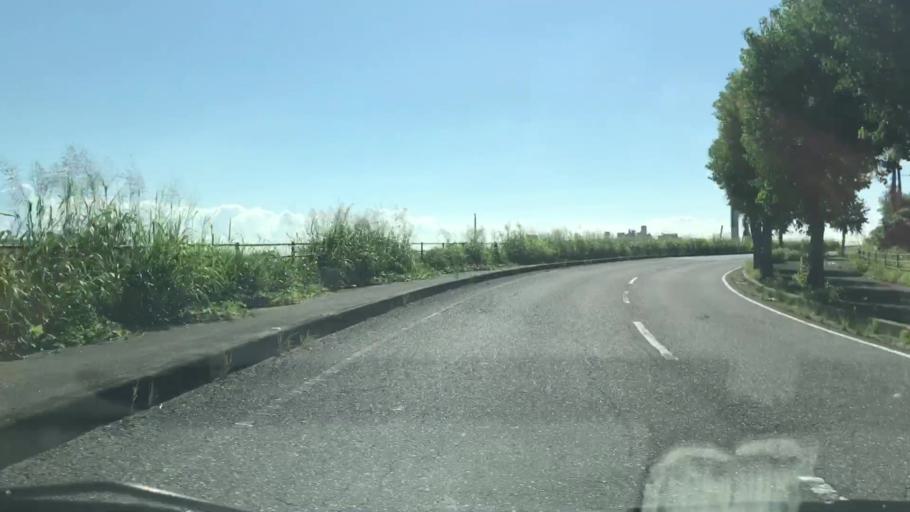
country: JP
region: Saga Prefecture
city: Okawa
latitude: 33.2278
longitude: 130.3721
